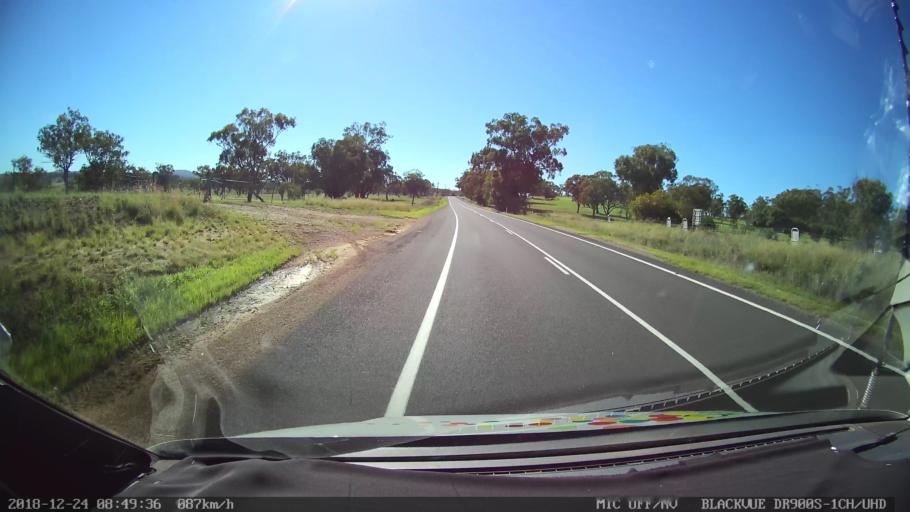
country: AU
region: New South Wales
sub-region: Liverpool Plains
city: Quirindi
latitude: -31.4685
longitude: 150.6558
